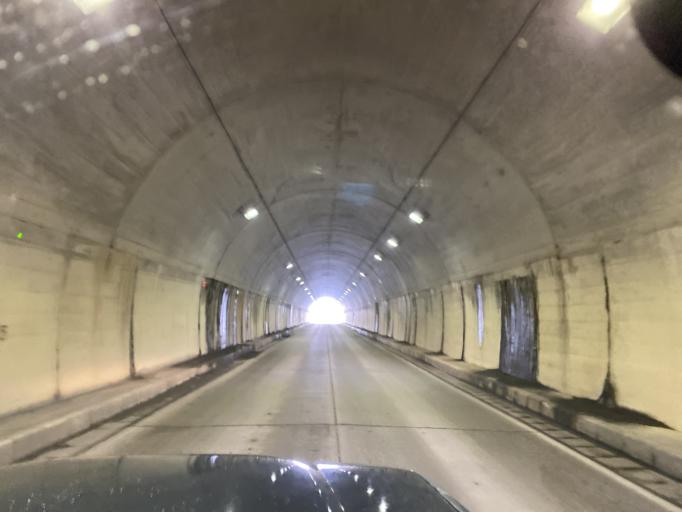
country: JP
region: Toyama
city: Fukumitsu
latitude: 36.3480
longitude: 136.8736
